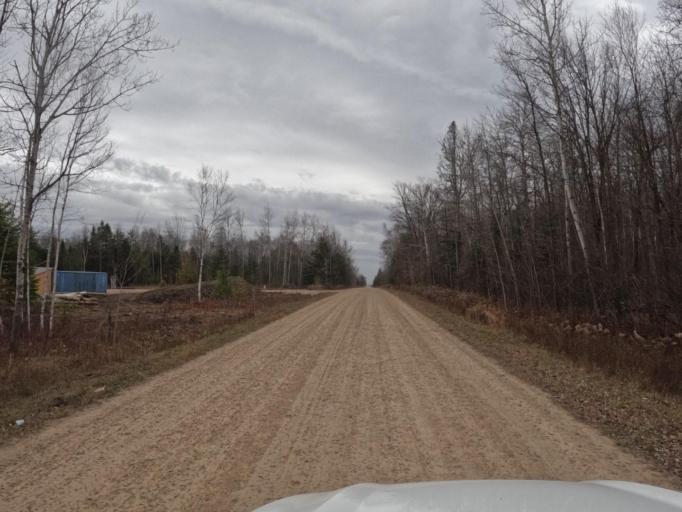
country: CA
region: Ontario
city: Shelburne
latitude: 44.0309
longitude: -80.3943
